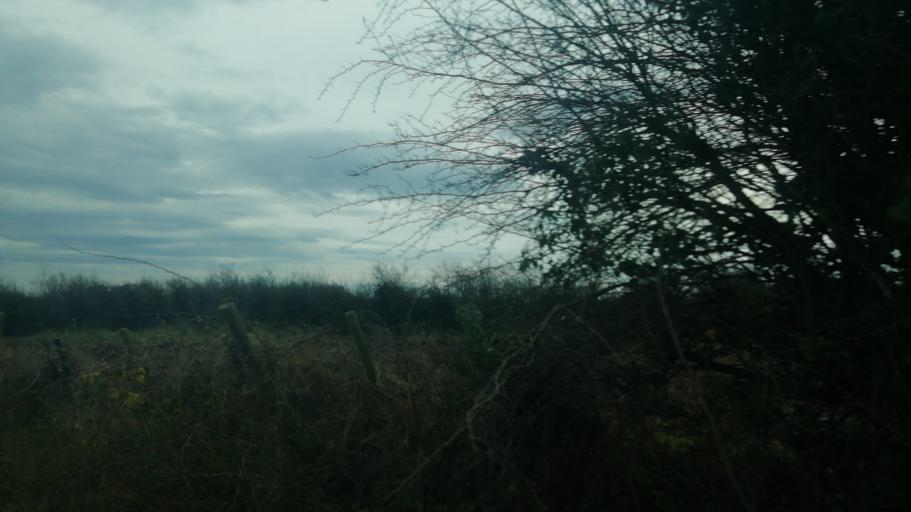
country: IE
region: Leinster
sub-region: Kildare
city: Clane
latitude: 53.3067
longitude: -6.7154
